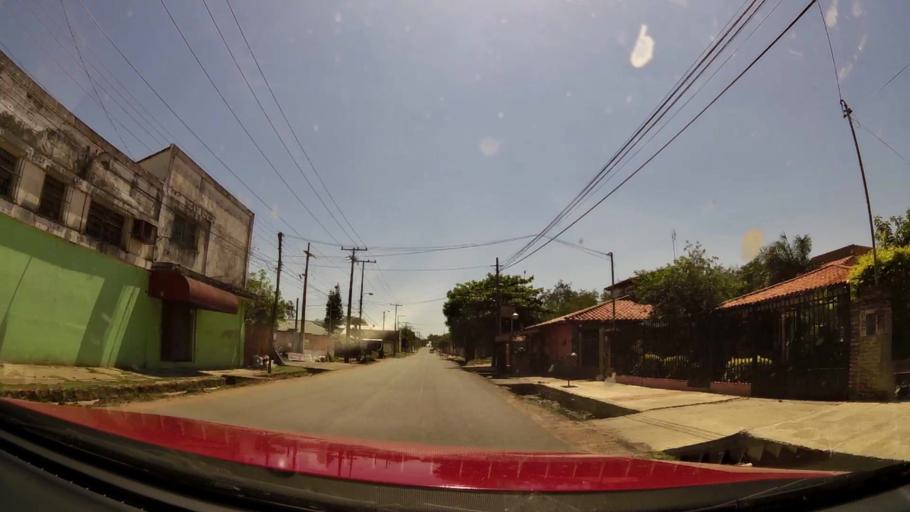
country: PY
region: Central
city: Colonia Mariano Roque Alonso
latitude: -25.2315
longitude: -57.5420
